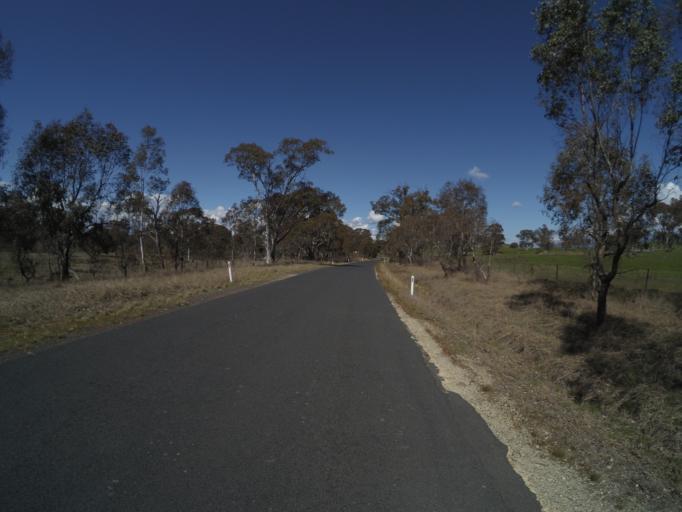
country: AU
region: New South Wales
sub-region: Yass Valley
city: Murrumbateman
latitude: -35.1010
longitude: 148.8621
